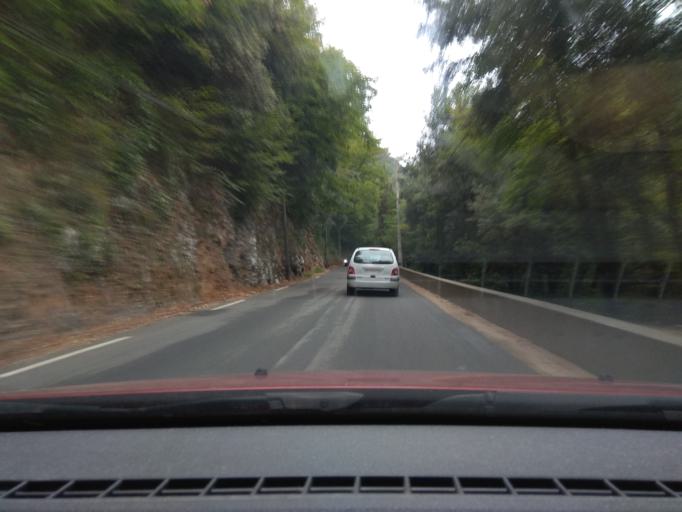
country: FR
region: Provence-Alpes-Cote d'Azur
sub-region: Departement des Alpes-Maritimes
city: La Colle-sur-Loup
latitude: 43.6805
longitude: 7.0787
